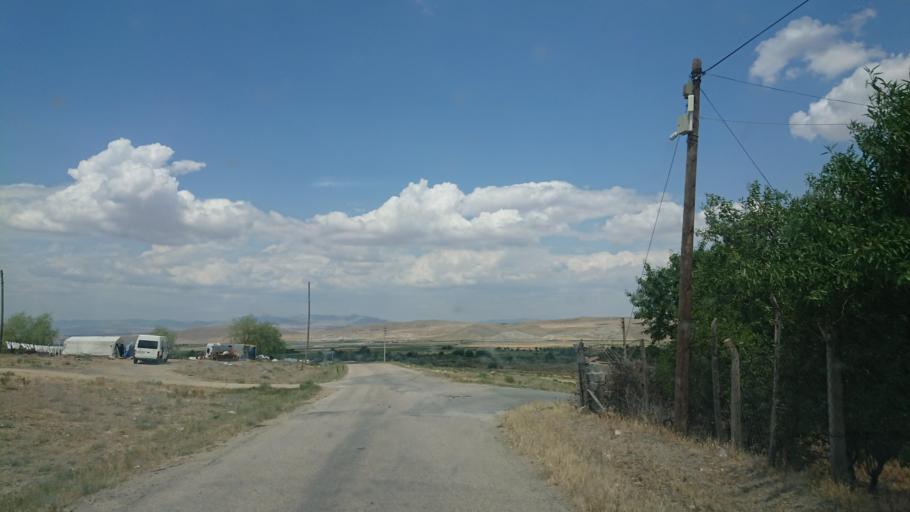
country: TR
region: Aksaray
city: Sariyahsi
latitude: 38.9632
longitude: 33.8886
